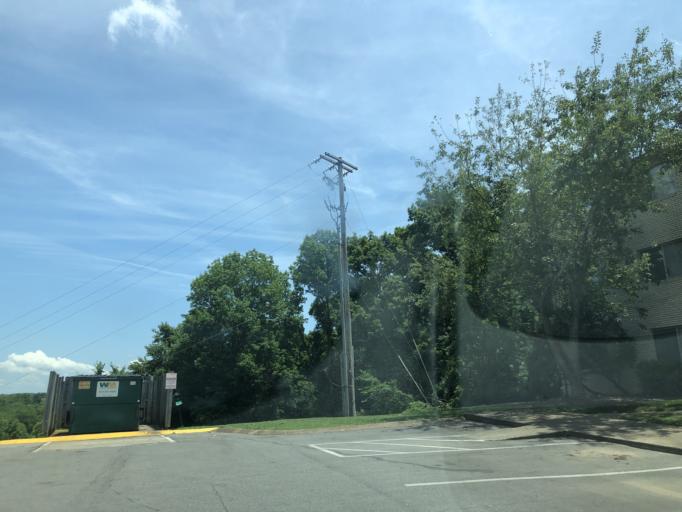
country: US
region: Tennessee
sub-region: Rutherford County
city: La Vergne
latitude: 36.0394
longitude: -86.6611
